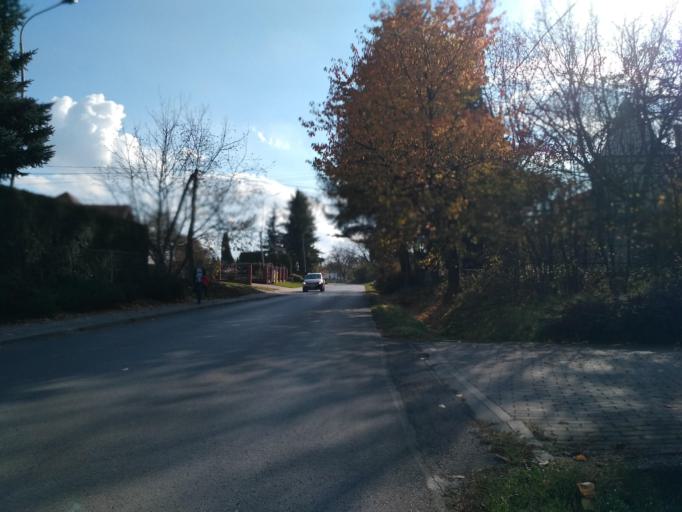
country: PL
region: Subcarpathian Voivodeship
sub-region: Powiat rzeszowski
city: Trzciana
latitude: 50.0741
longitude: 21.8360
